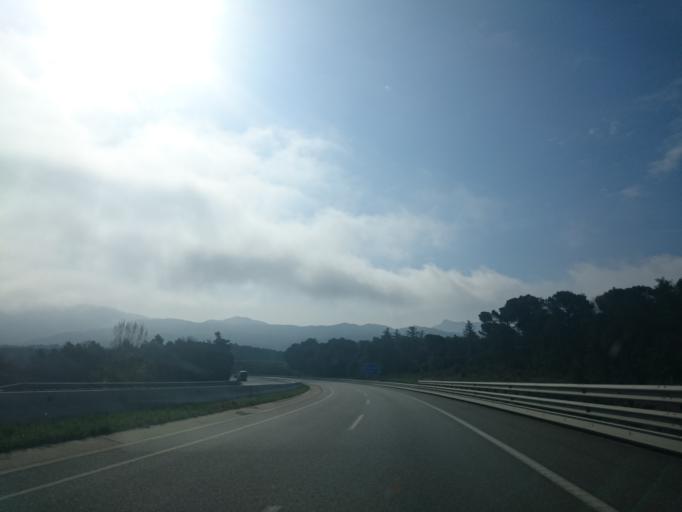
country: ES
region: Catalonia
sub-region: Provincia de Barcelona
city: Sant Julia de Vilatorta
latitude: 41.8953
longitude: 2.3460
